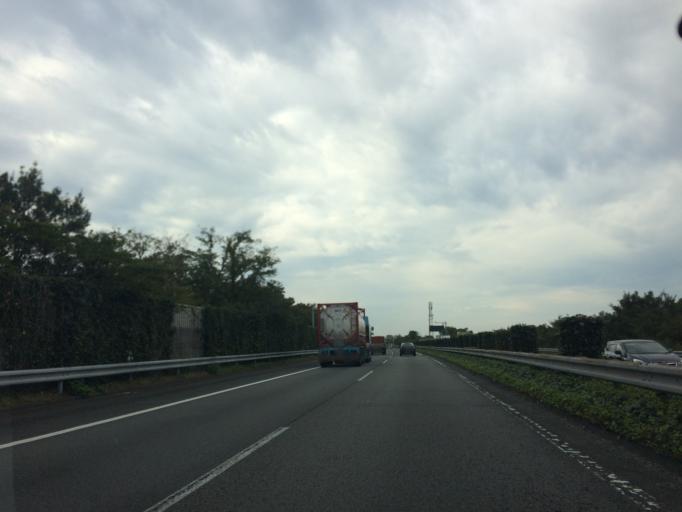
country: JP
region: Shizuoka
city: Yaizu
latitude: 34.8793
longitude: 138.2973
